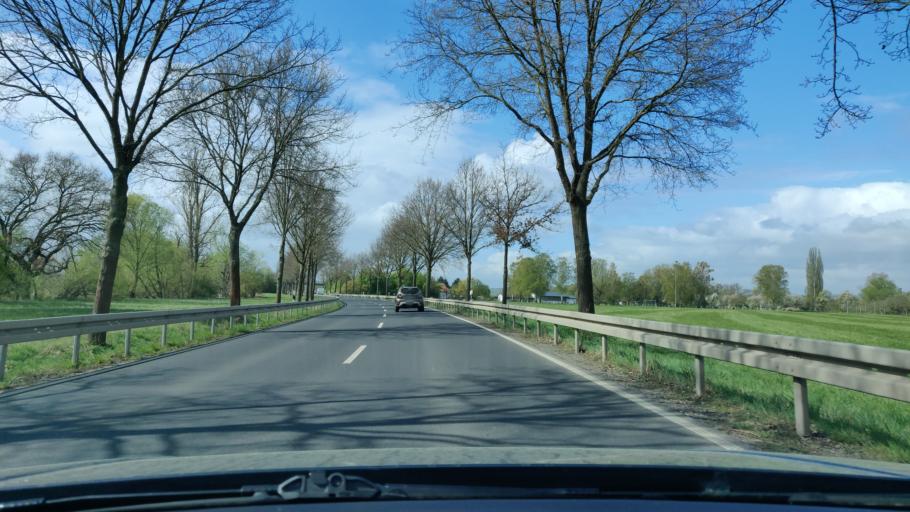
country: DE
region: Hesse
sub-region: Regierungsbezirk Kassel
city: Wabern
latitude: 51.1034
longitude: 9.3832
